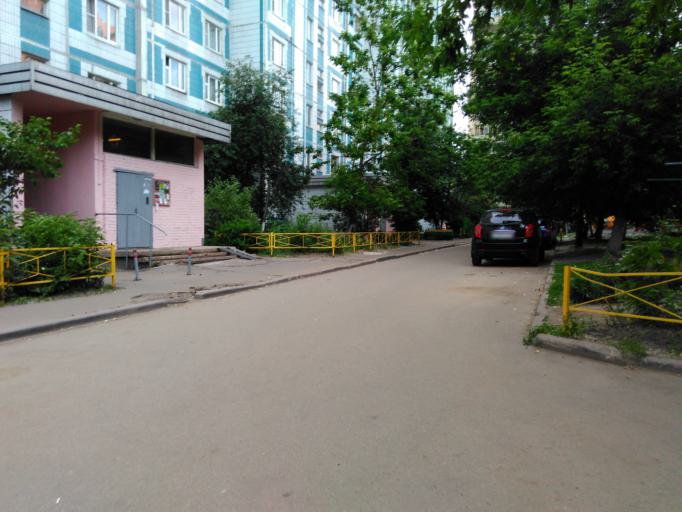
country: RU
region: Moskovskaya
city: Reutov
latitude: 55.7466
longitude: 37.8639
